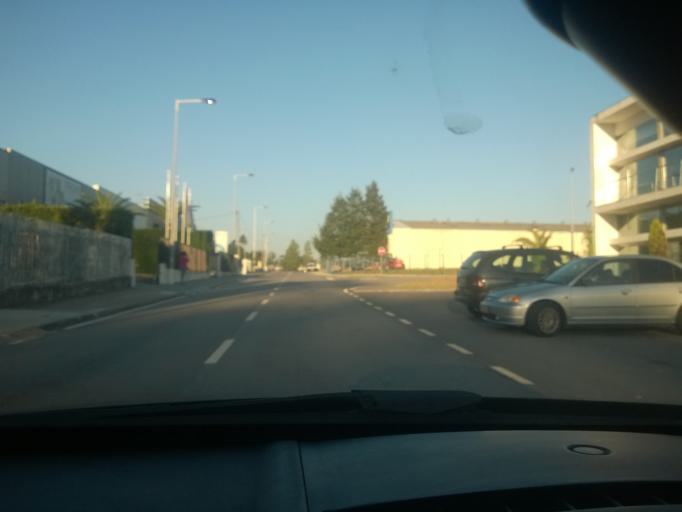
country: PT
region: Porto
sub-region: Maia
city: Gemunde
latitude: 41.2618
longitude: -8.6384
